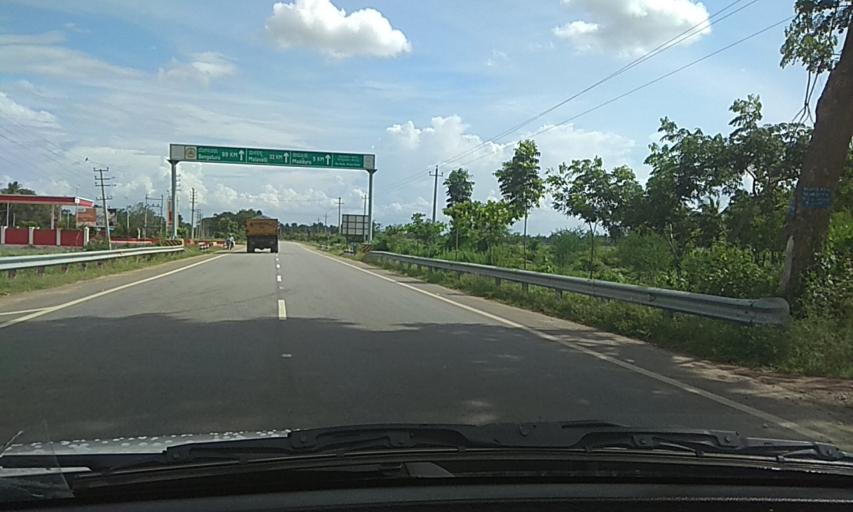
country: IN
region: Karnataka
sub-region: Mandya
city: Maddur
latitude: 12.6575
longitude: 77.0530
